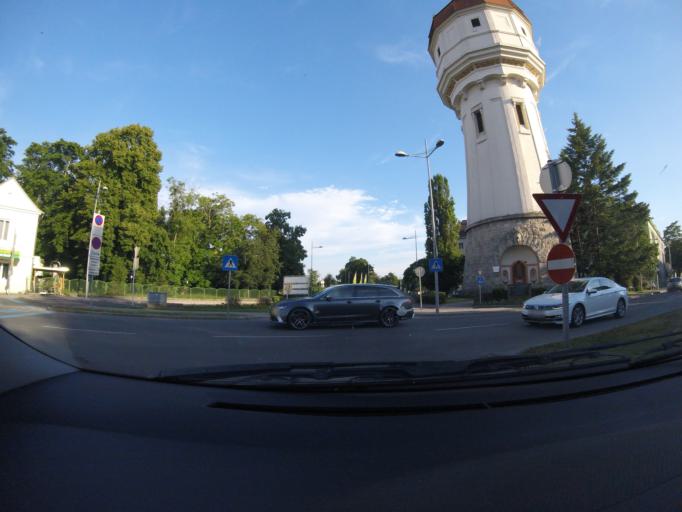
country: AT
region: Lower Austria
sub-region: Wiener Neustadt Stadt
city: Wiener Neustadt
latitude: 47.8080
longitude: 16.2432
